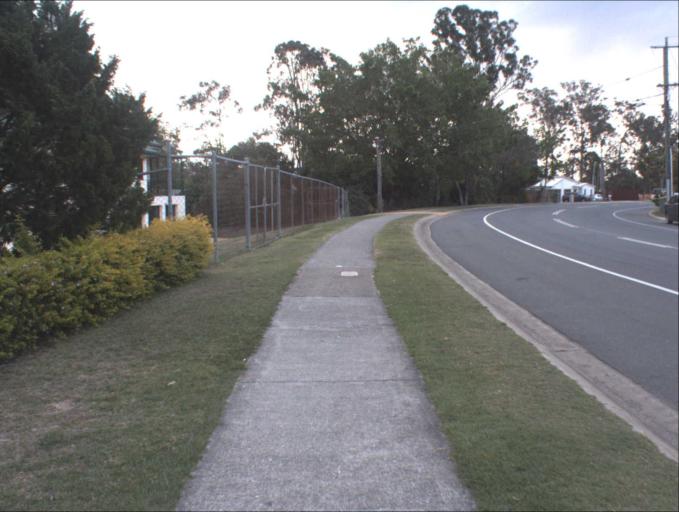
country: AU
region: Queensland
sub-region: Logan
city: Waterford West
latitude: -27.6811
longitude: 153.1315
